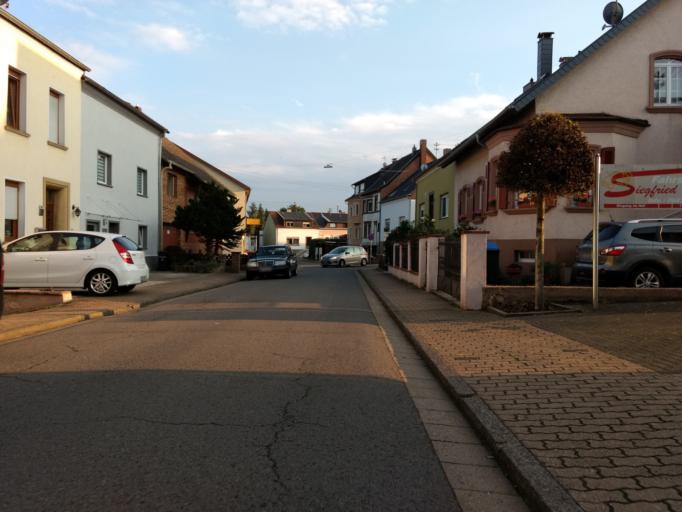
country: DE
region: Saarland
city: Nalbach
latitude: 49.3779
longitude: 6.7864
